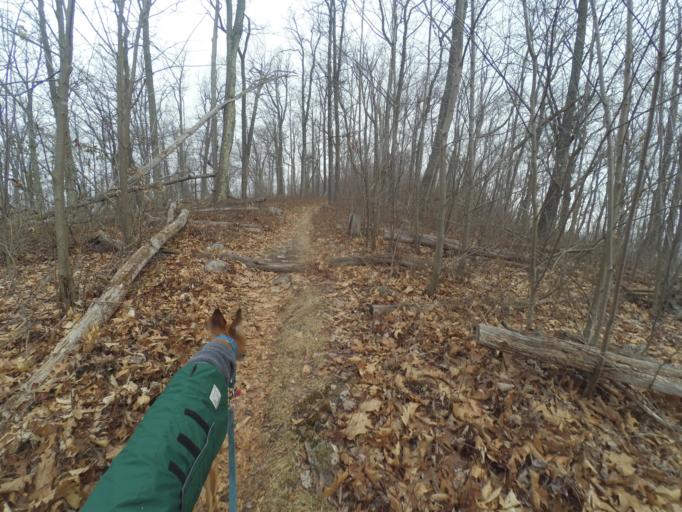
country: US
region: Pennsylvania
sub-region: Centre County
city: Boalsburg
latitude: 40.7631
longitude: -77.7151
